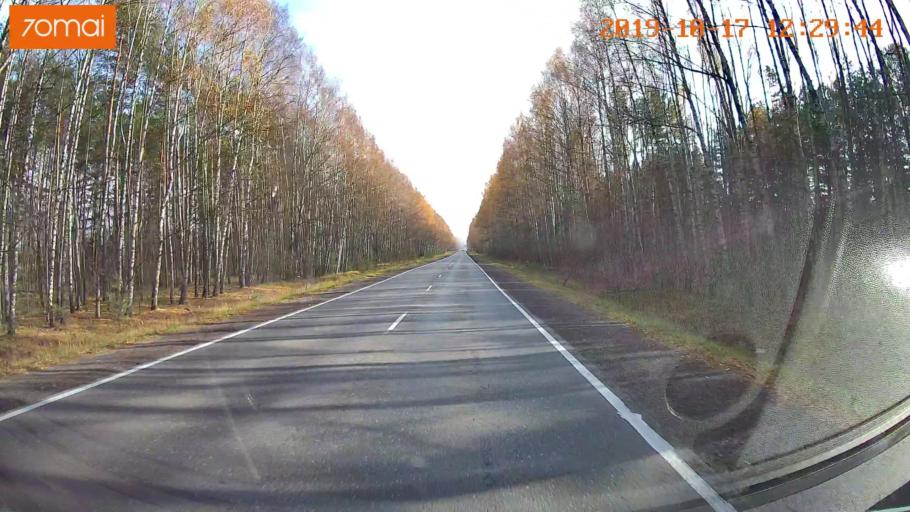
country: RU
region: Rjazan
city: Syntul
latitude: 54.9795
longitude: 41.2993
